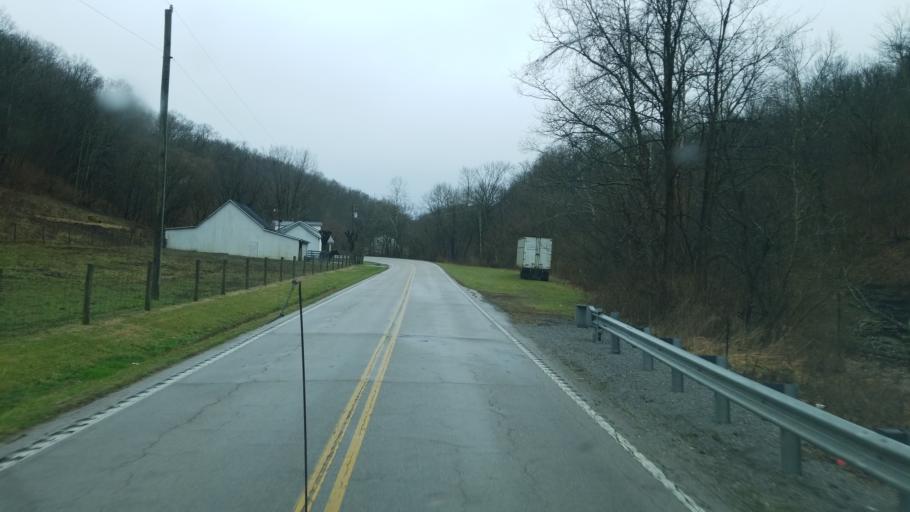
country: US
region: Kentucky
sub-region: Mason County
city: Maysville
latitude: 38.6232
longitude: -83.7038
